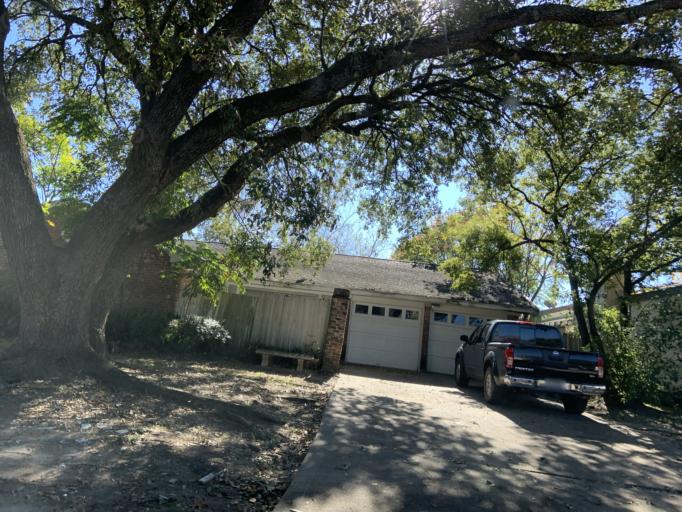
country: US
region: Texas
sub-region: Harris County
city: Bellaire
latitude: 29.6860
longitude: -95.5051
